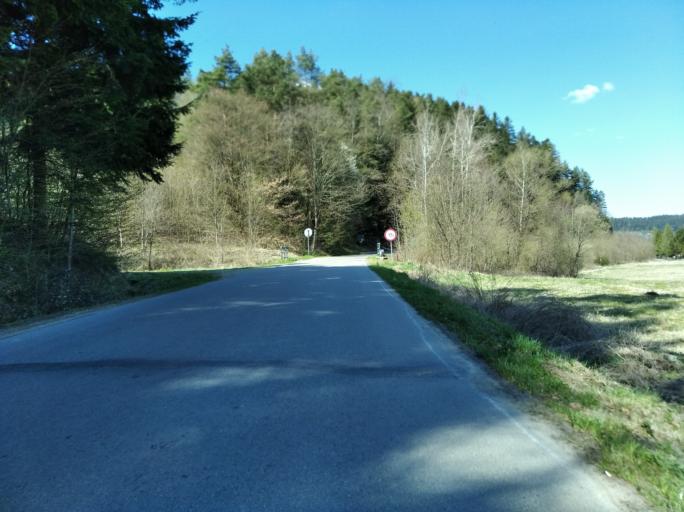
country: PL
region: Subcarpathian Voivodeship
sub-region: Powiat brzozowski
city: Dydnia
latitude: 49.6908
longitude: 22.2071
